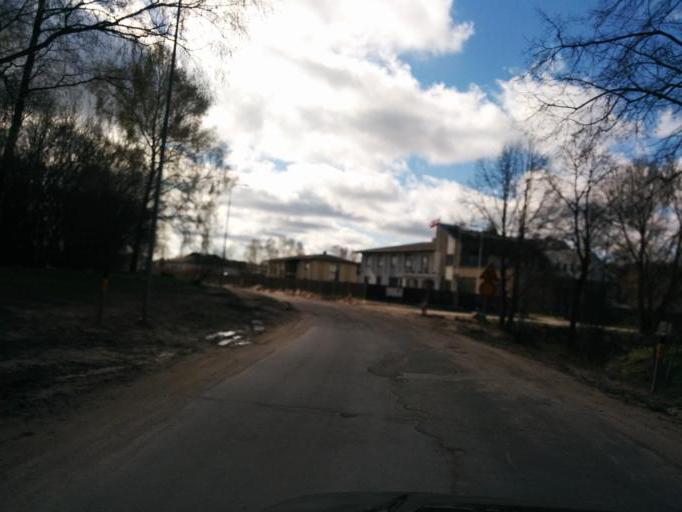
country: LV
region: Kekava
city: Balozi
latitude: 56.8868
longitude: 24.1580
